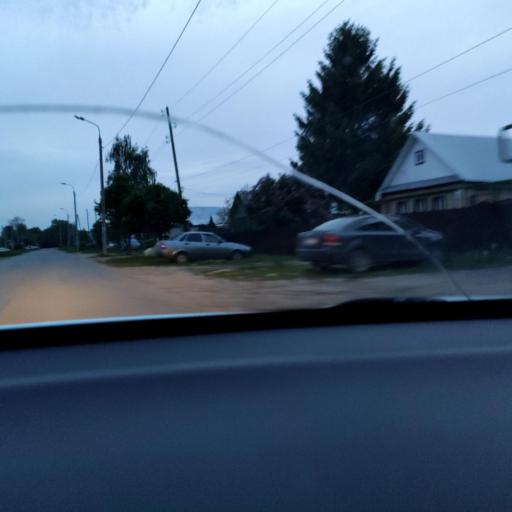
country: RU
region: Tatarstan
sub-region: Gorod Kazan'
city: Kazan
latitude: 55.7014
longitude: 49.0730
